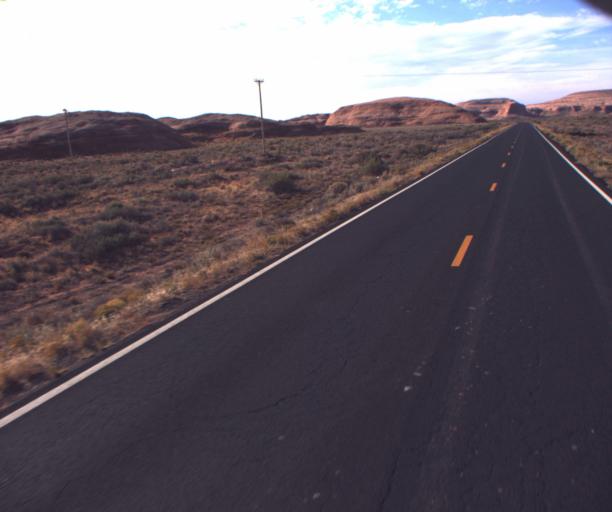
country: US
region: Arizona
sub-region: Apache County
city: Many Farms
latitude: 36.7792
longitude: -109.6588
